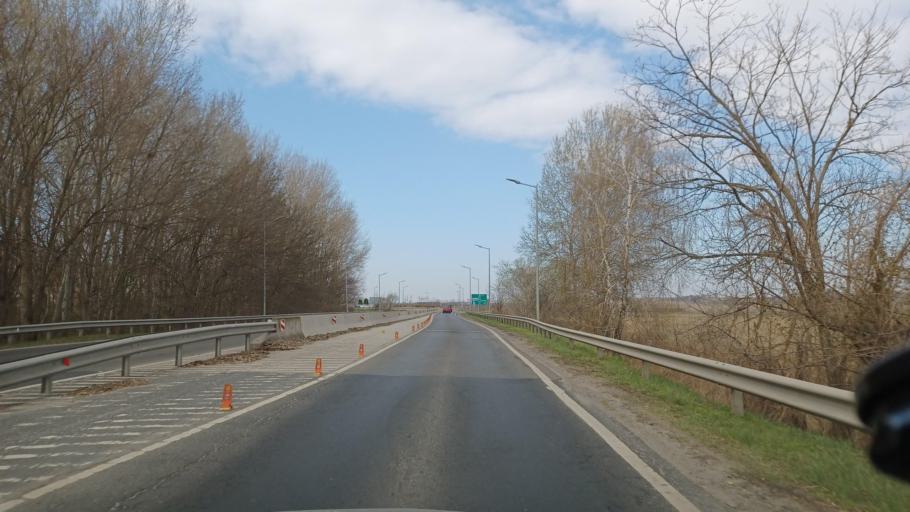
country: HU
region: Tolna
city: Szekszard
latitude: 46.3768
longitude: 18.6807
